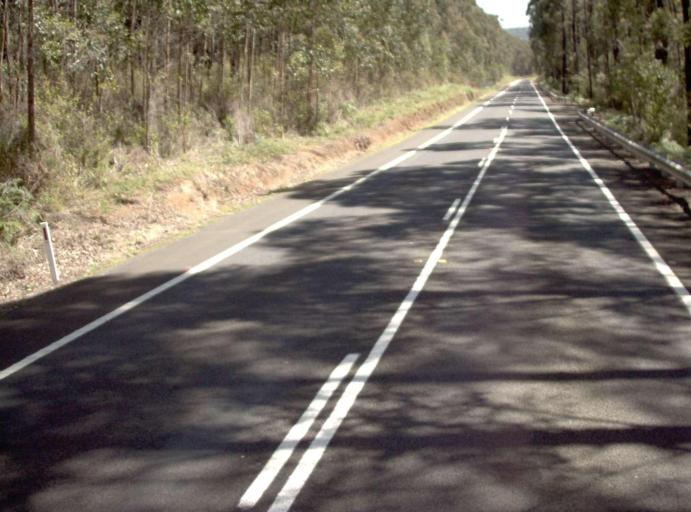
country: AU
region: New South Wales
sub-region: Bombala
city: Bombala
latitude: -37.5710
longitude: 149.0272
